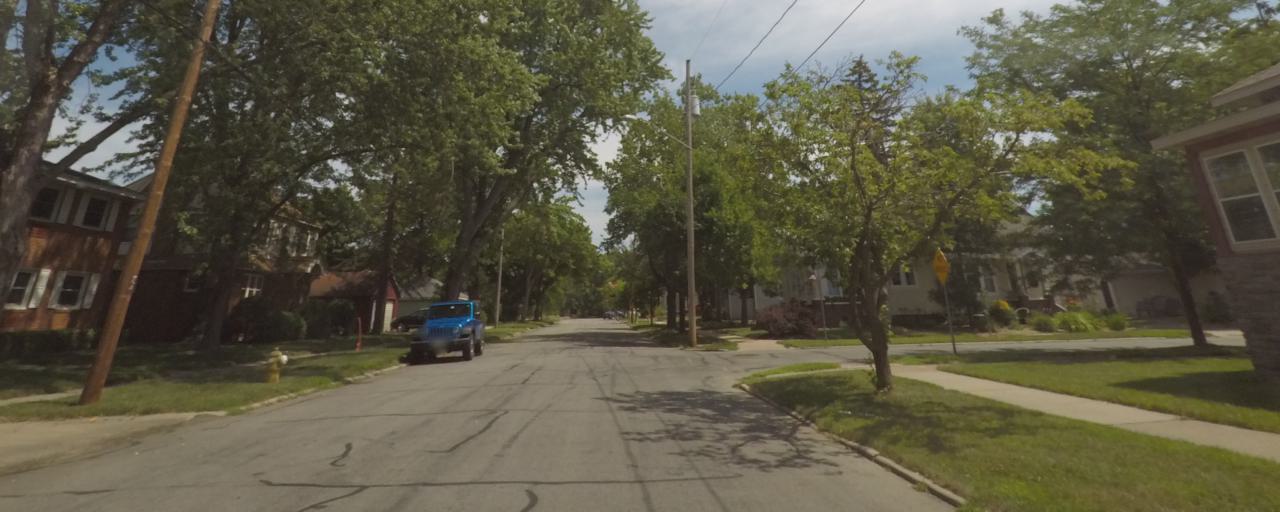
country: US
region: Wisconsin
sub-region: Portage County
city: Stevens Point
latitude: 44.5208
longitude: -89.5764
